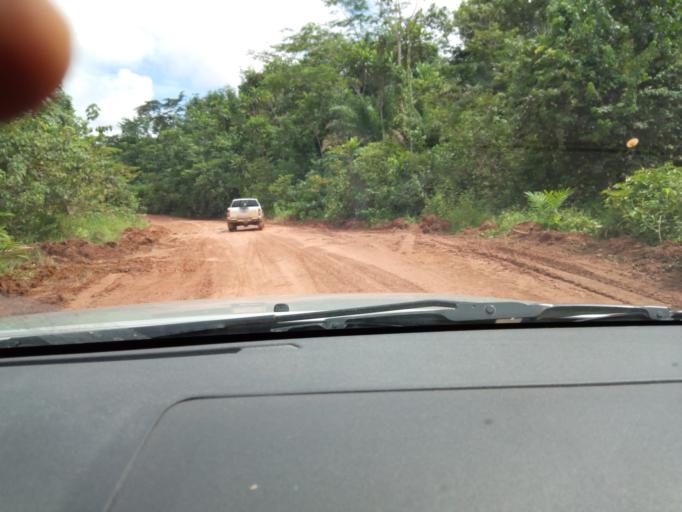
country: CI
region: Dix-Huit Montagnes
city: Toulepleu Guere
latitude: 6.7651
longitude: -8.7848
